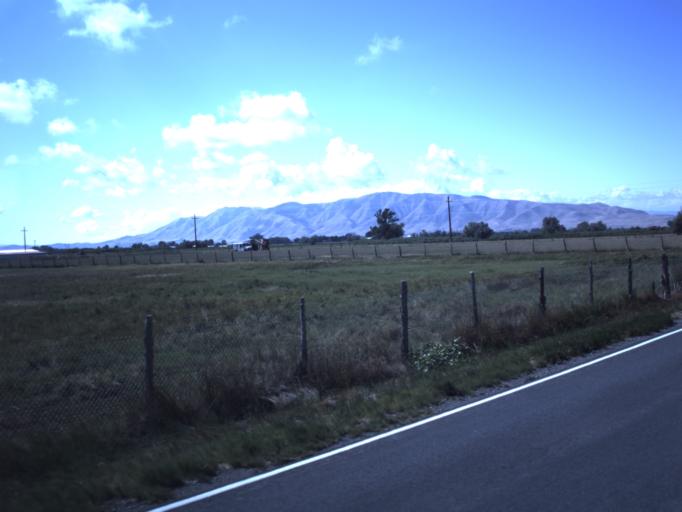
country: US
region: Utah
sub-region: Utah County
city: Spanish Fork
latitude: 40.1585
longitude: -111.6947
